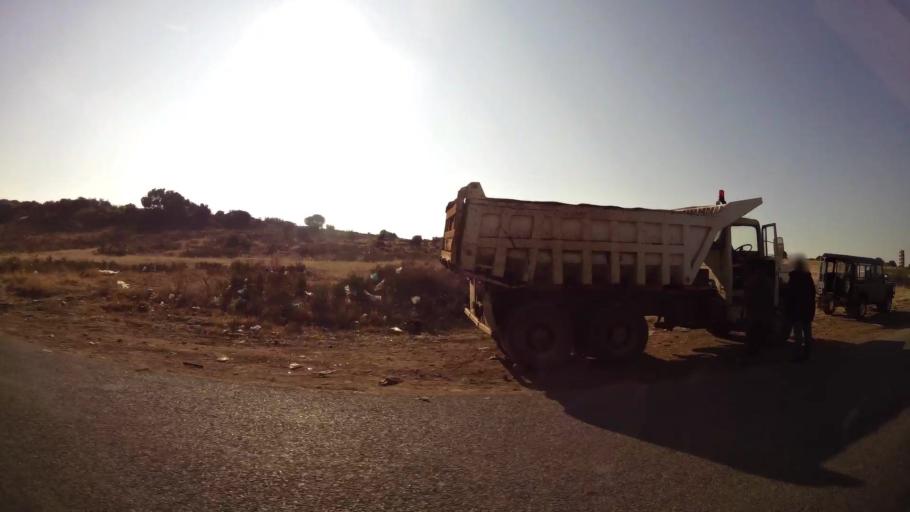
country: ZA
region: Orange Free State
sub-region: Mangaung Metropolitan Municipality
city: Bloemfontein
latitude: -29.1799
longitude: 26.1980
